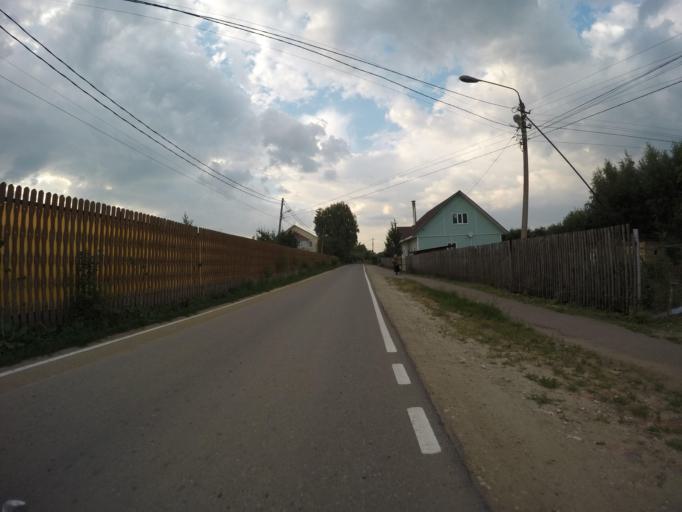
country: RU
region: Moskovskaya
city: Rechitsy
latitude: 55.5958
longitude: 38.5051
